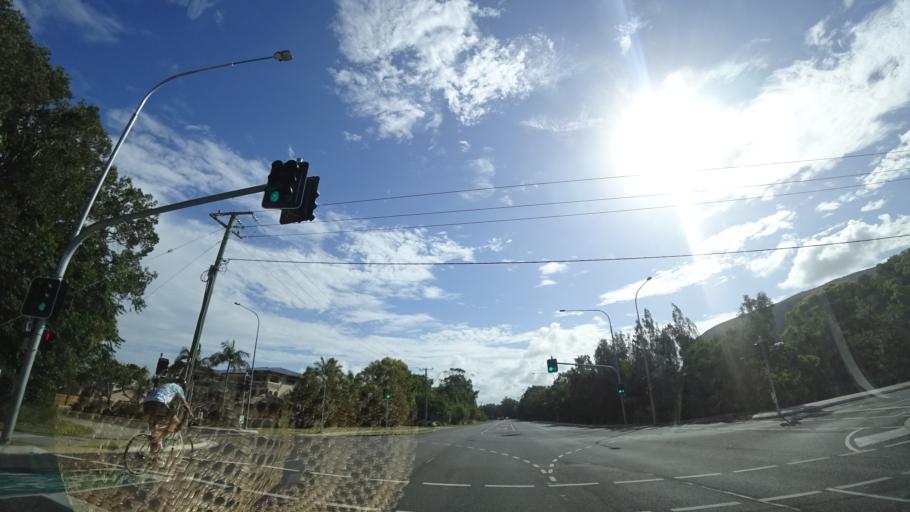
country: AU
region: Queensland
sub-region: Sunshine Coast
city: Coolum Beach
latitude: -26.5624
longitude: 153.0946
